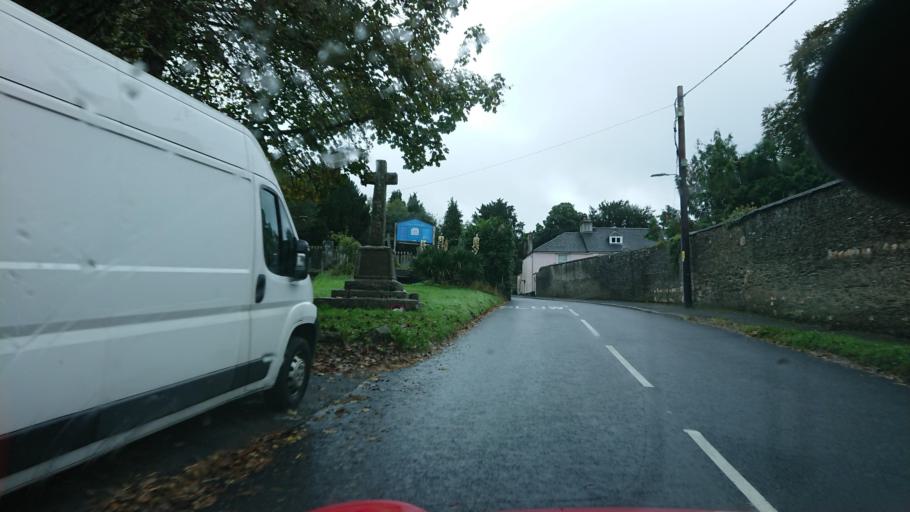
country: GB
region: England
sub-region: Plymouth
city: Plymouth
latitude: 50.4272
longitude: -4.1542
